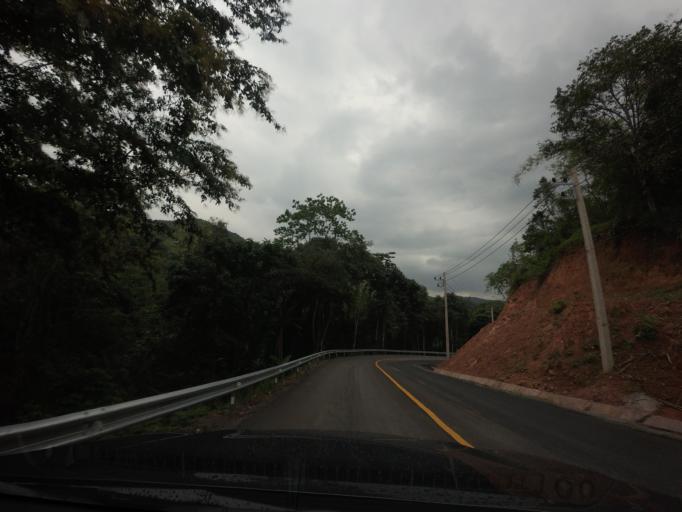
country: TH
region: Nan
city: Bo Kluea
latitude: 19.1875
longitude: 101.1802
